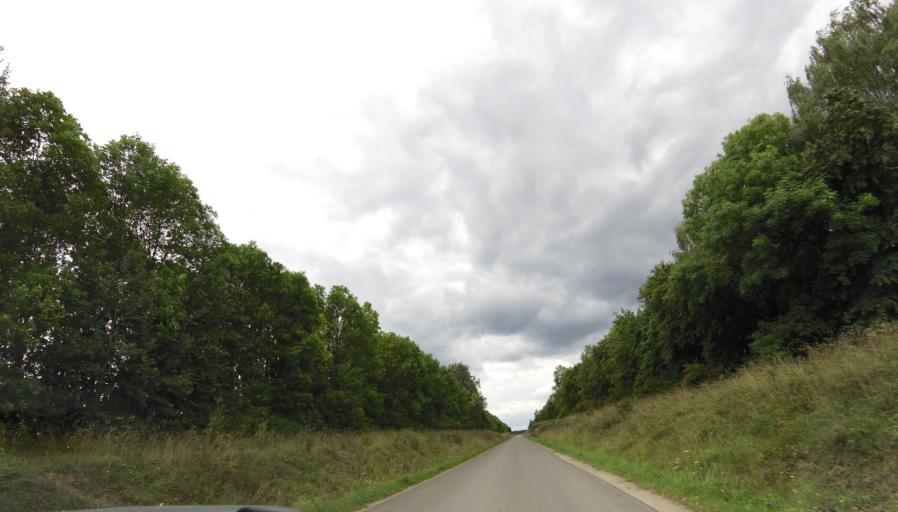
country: LT
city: Linkuva
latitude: 56.0571
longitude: 24.1623
